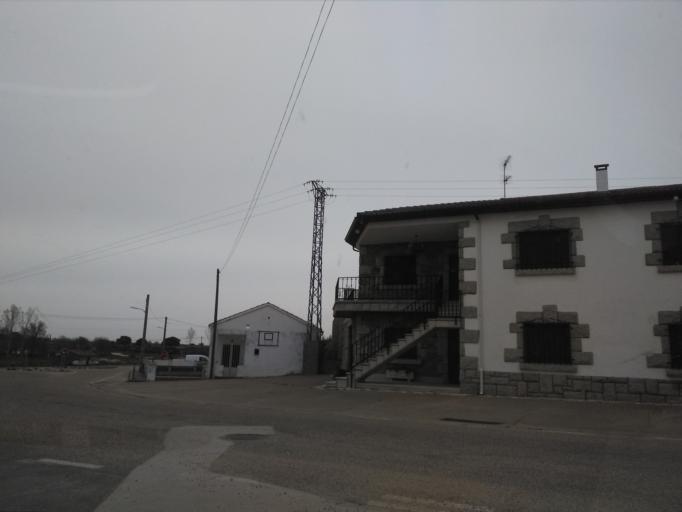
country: ES
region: Castille and Leon
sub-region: Provincia de Salamanca
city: Yecla de Yeltes
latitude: 40.9610
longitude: -6.4887
